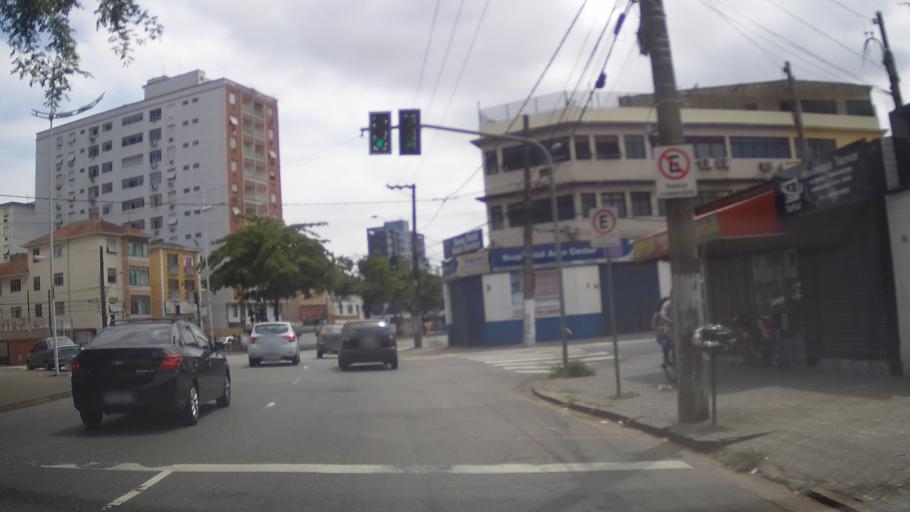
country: BR
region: Sao Paulo
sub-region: Santos
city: Santos
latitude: -23.9643
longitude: -46.3114
